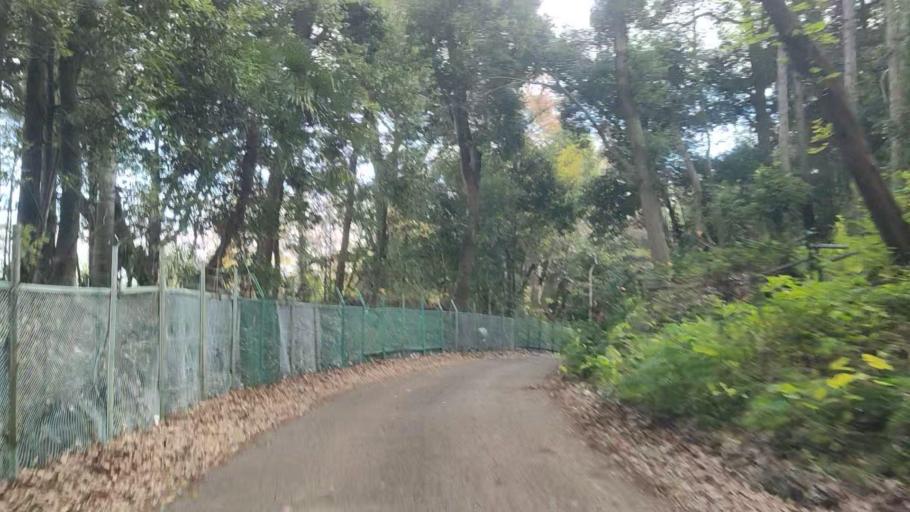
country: JP
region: Kanagawa
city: Minami-rinkan
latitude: 35.4838
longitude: 139.4981
